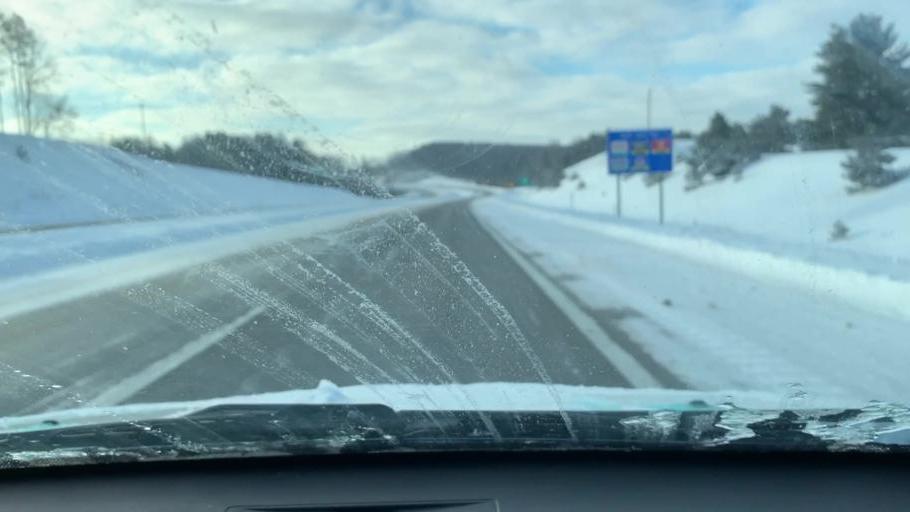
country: US
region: Michigan
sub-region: Wexford County
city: Cadillac
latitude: 44.3042
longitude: -85.3924
